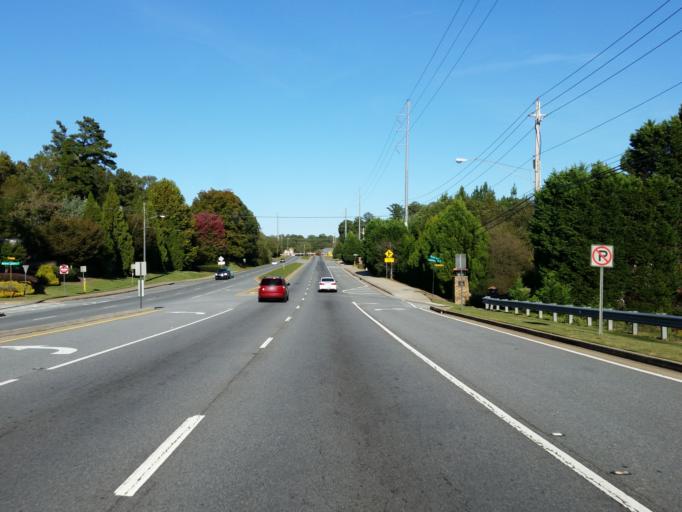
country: US
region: Georgia
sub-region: Cobb County
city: Marietta
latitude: 33.9767
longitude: -84.4687
